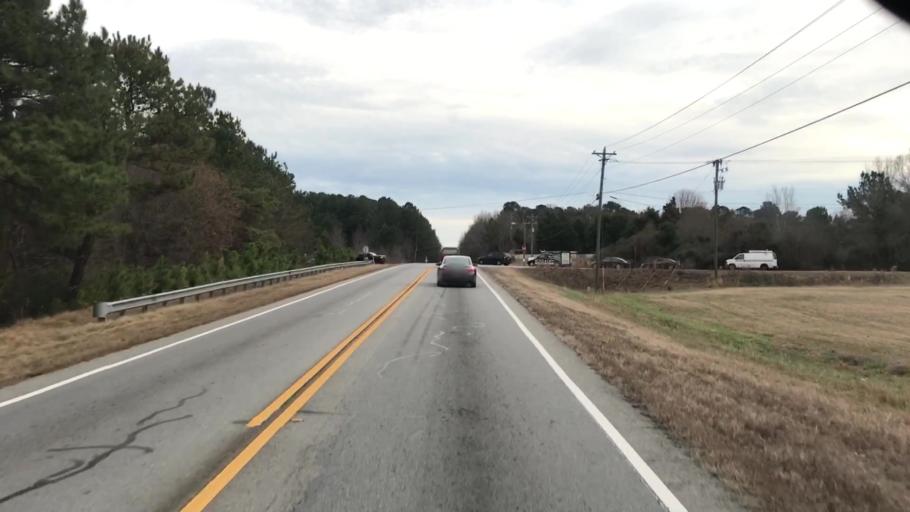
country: US
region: Georgia
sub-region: Jackson County
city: Hoschton
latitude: 34.0707
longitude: -83.7870
